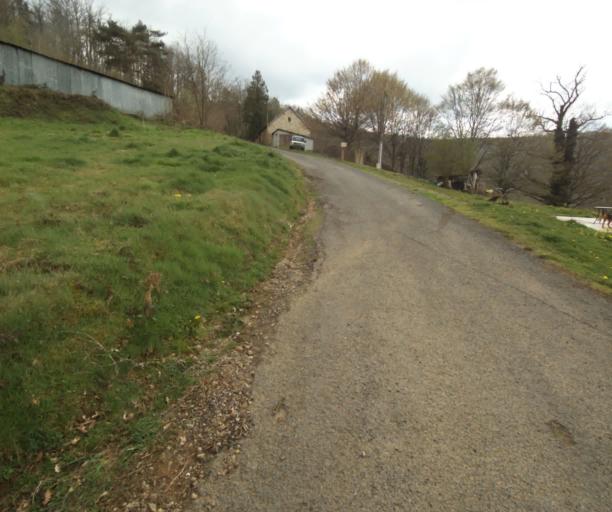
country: FR
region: Limousin
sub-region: Departement de la Correze
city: Naves
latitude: 45.3197
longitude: 1.8099
